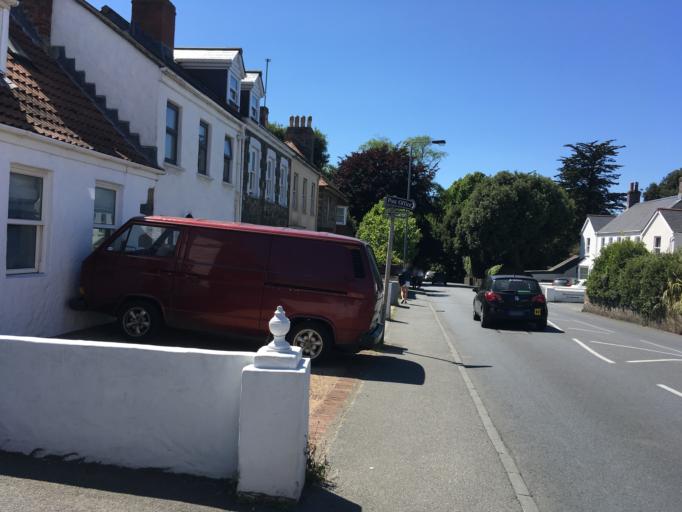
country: GG
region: St Peter Port
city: Saint Peter Port
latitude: 49.4601
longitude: -2.5599
